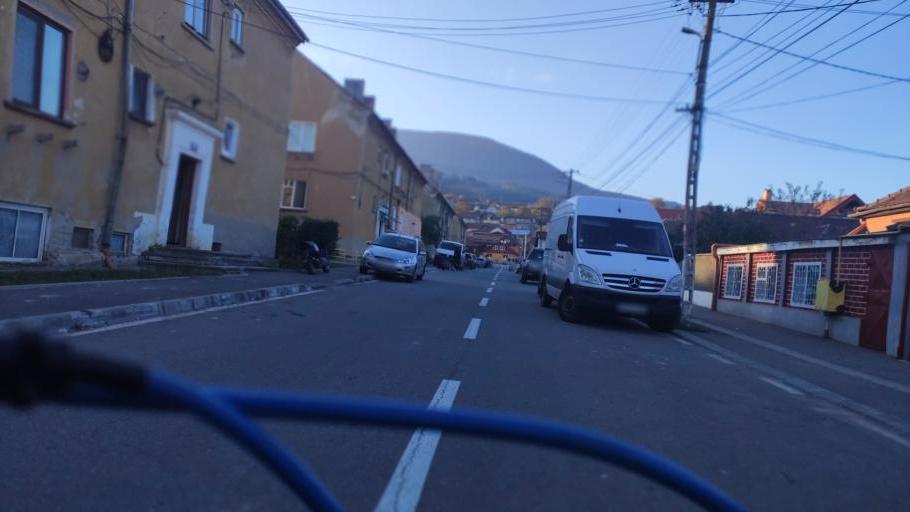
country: RO
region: Brasov
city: Codlea
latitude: 45.6913
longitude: 25.4415
